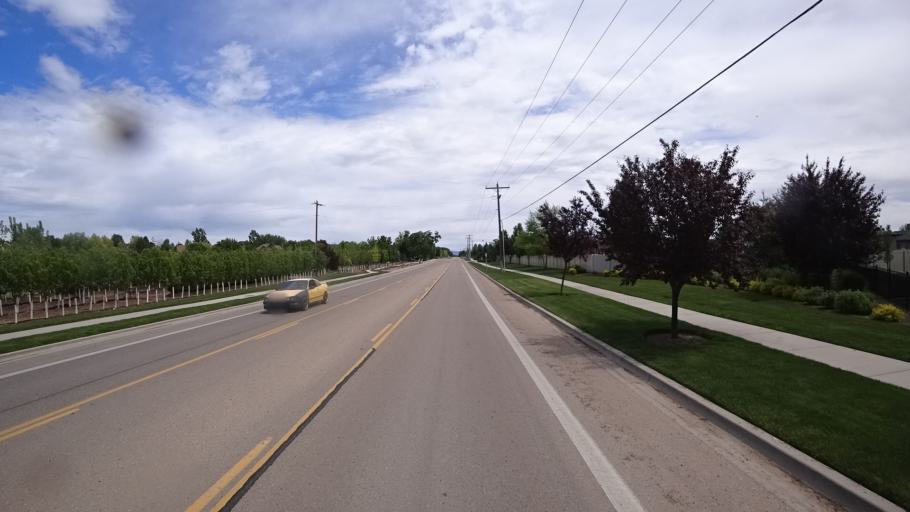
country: US
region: Idaho
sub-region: Ada County
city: Meridian
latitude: 43.5756
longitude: -116.3904
